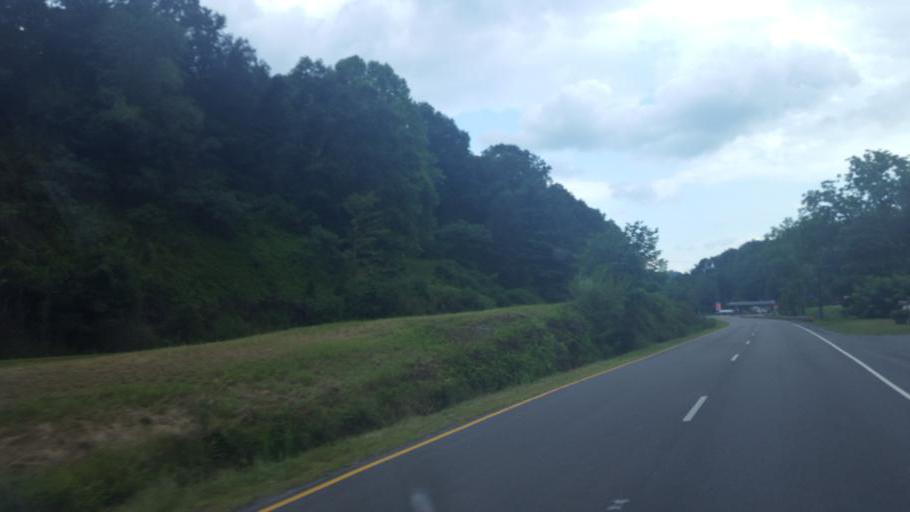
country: US
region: Virginia
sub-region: Wise County
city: Pound
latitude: 37.0927
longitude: -82.6002
